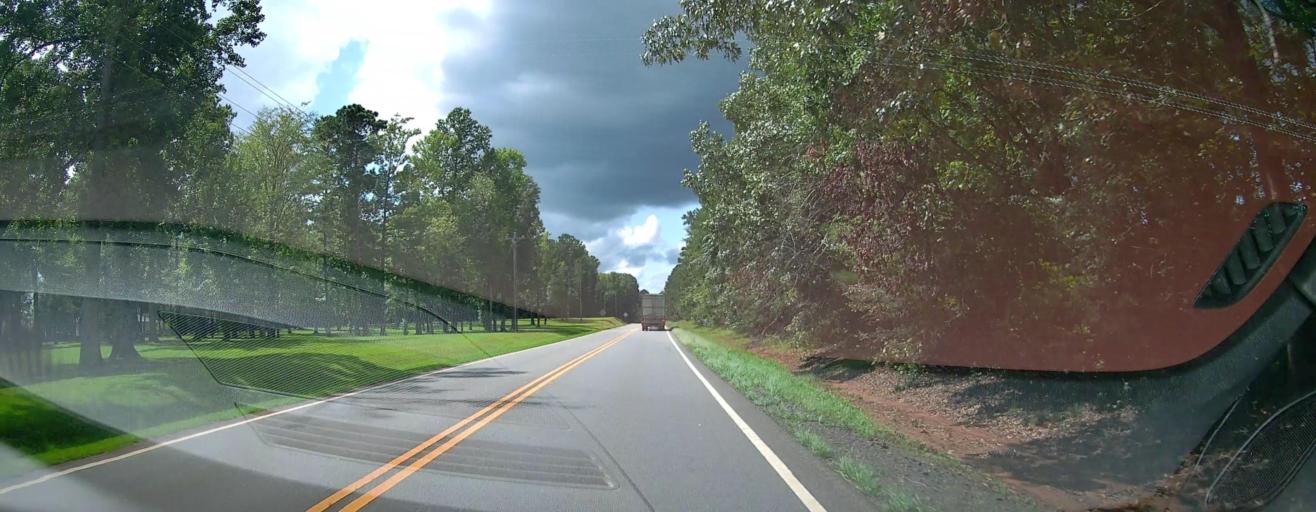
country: US
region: Georgia
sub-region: Bibb County
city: West Point
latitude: 32.8652
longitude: -83.8972
